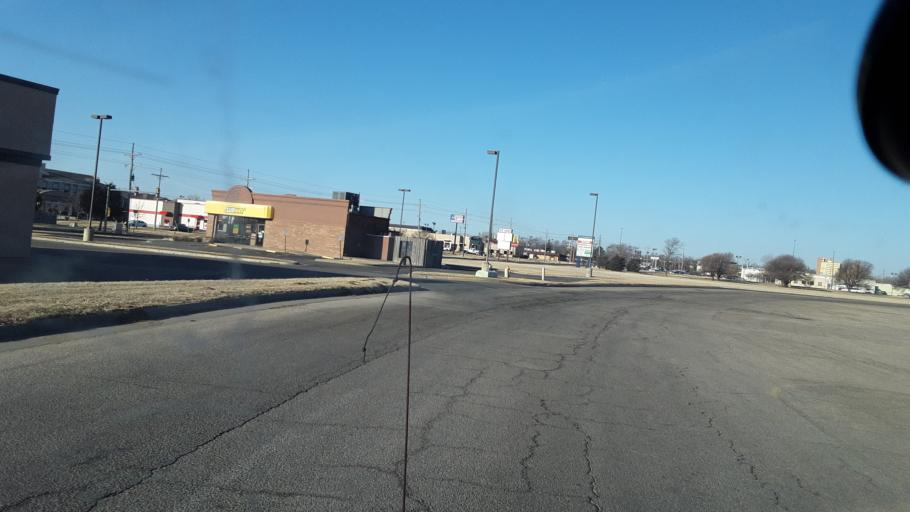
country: US
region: Kansas
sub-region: Reno County
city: Hutchinson
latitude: 38.0656
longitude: -97.8982
